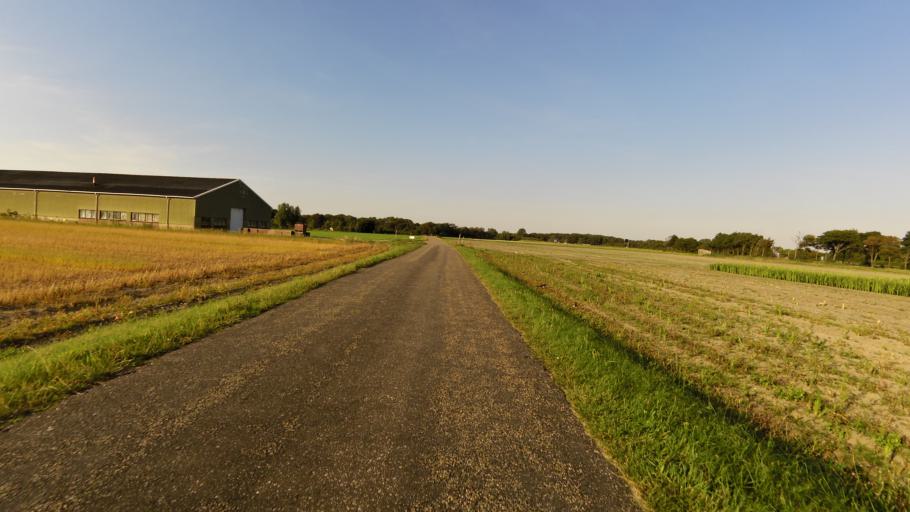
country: NL
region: South Holland
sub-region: Gemeente Noordwijk
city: Noordwijk-Binnen
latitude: 52.2372
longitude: 4.4659
